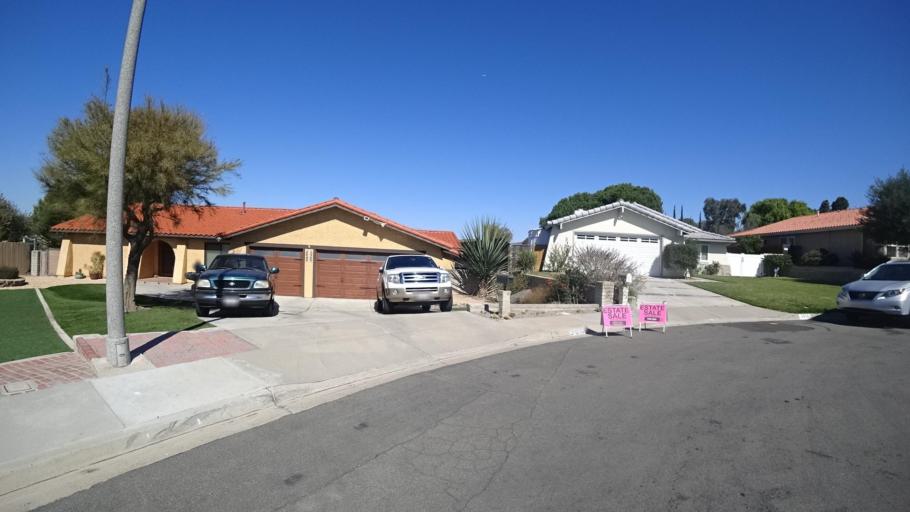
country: US
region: California
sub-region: San Diego County
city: Bonita
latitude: 32.6713
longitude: -117.0100
